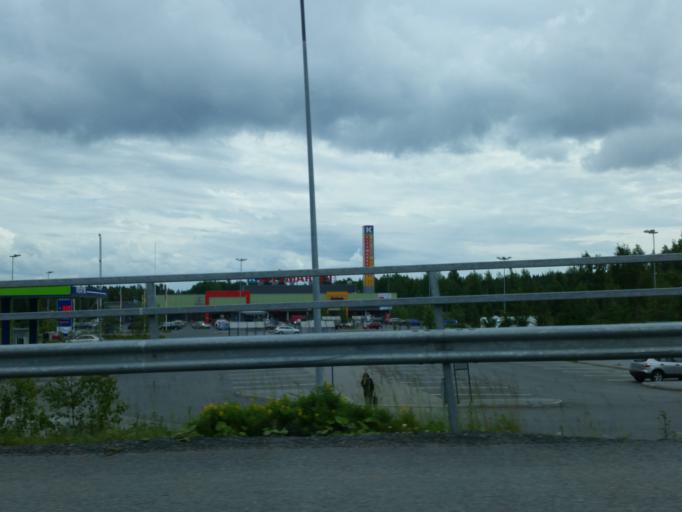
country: FI
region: Northern Savo
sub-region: Kuopio
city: Kuopio
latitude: 62.9344
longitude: 27.6697
